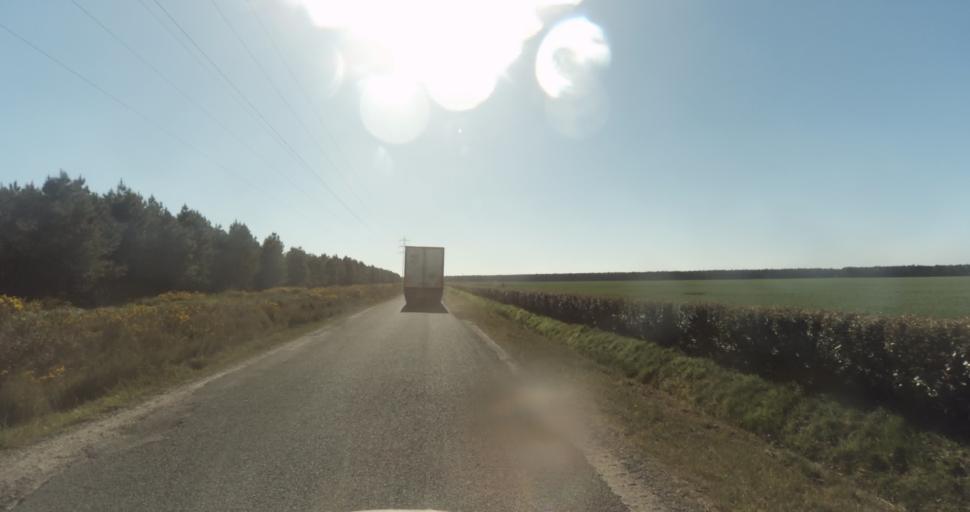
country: FR
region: Aquitaine
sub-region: Departement de la Gironde
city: Marcheprime
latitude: 44.7444
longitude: -0.8318
